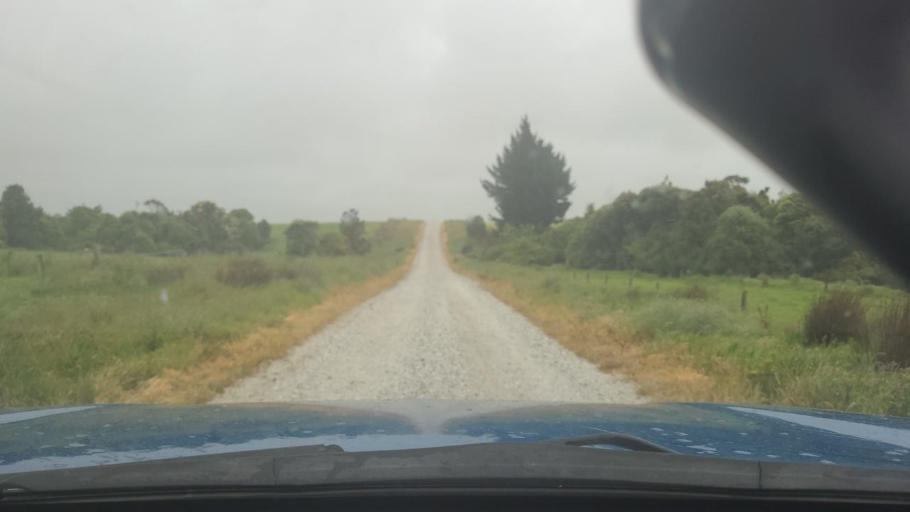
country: NZ
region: Southland
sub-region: Invercargill City
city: Invercargill
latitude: -46.4228
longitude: 168.7117
